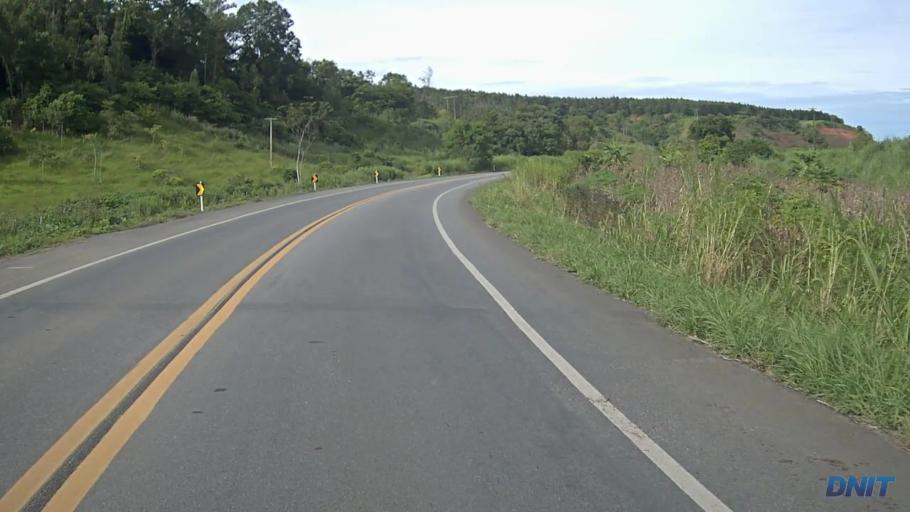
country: BR
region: Minas Gerais
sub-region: Belo Oriente
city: Belo Oriente
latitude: -19.2699
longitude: -42.3563
